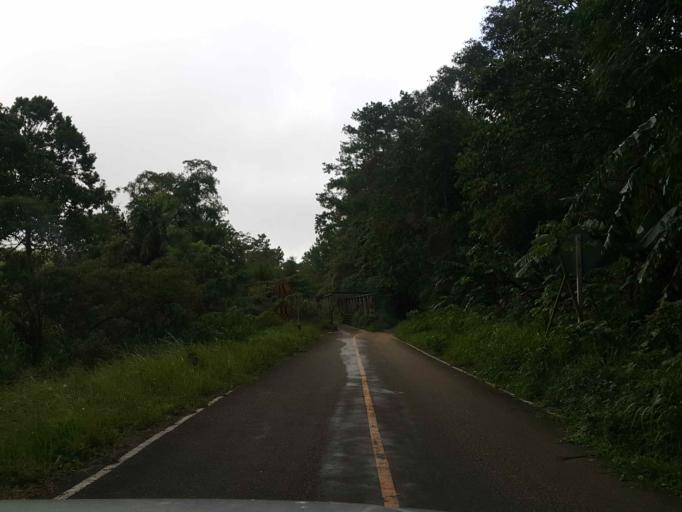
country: TH
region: Tak
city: Tak
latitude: 16.7814
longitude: 98.9271
